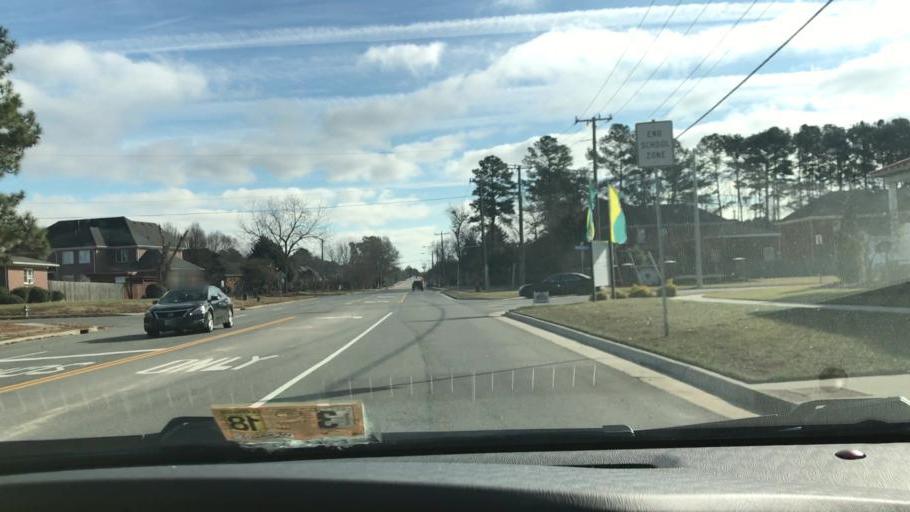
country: US
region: Virginia
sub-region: City of Chesapeake
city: Chesapeake
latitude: 36.6901
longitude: -76.2369
